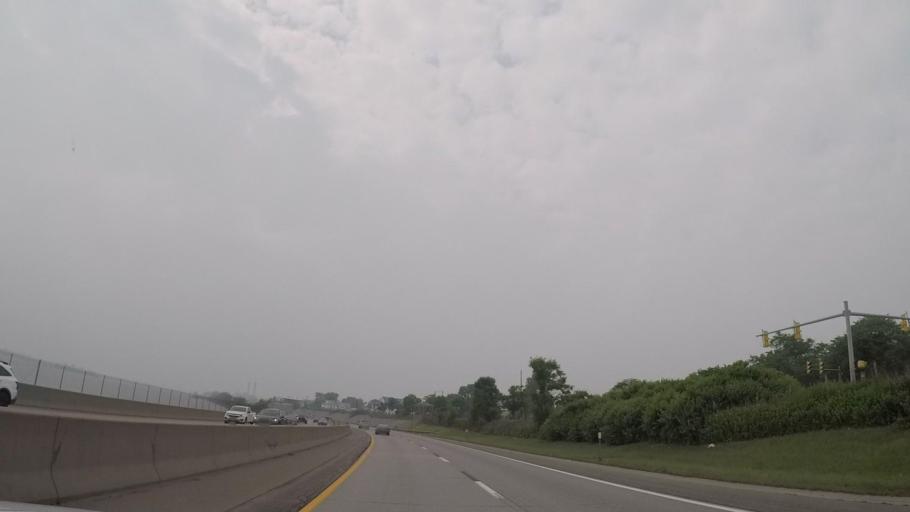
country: US
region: New York
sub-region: Erie County
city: Kenmore
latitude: 42.9546
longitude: -78.9106
